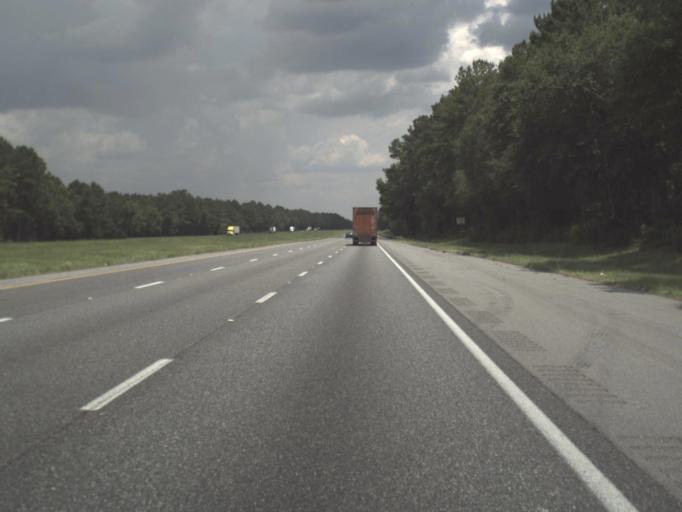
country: US
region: Florida
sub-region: Suwannee County
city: Wellborn
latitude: 30.3633
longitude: -82.8510
